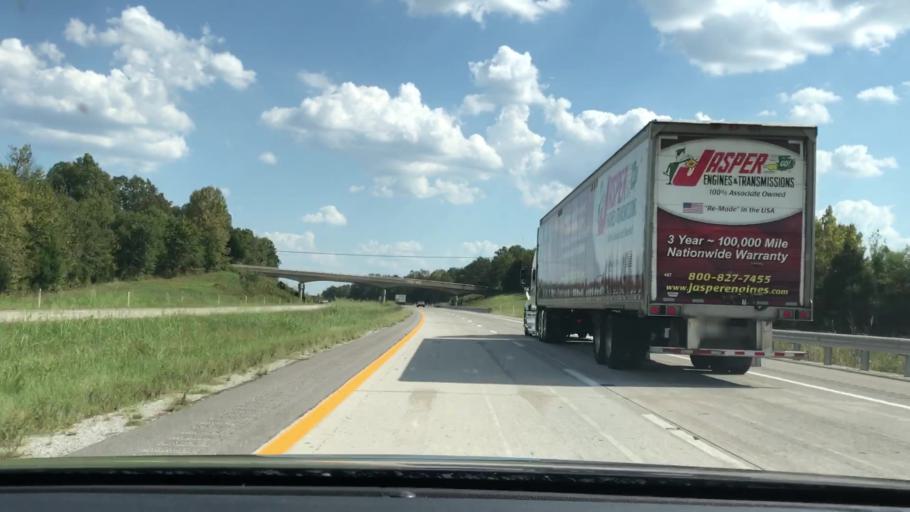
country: US
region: Kentucky
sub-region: Ohio County
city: Oak Grove
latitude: 37.3523
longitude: -86.7865
